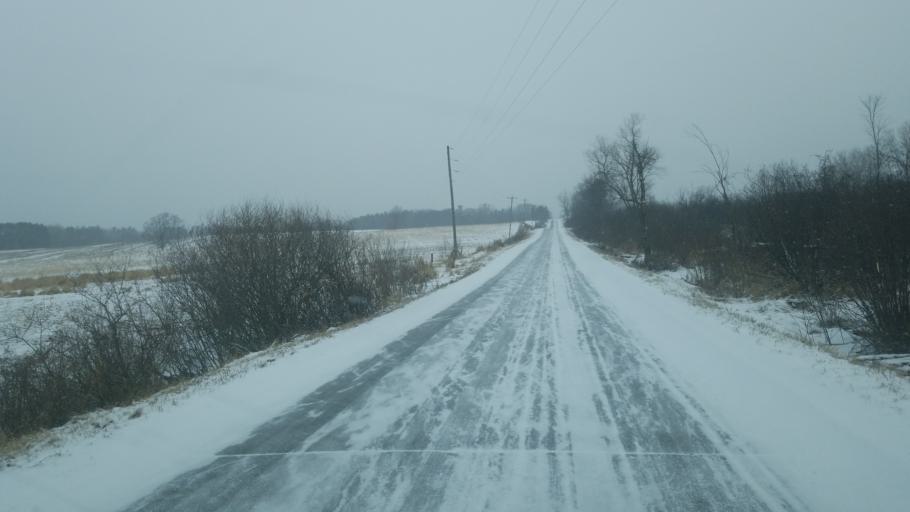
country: US
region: Michigan
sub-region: Mecosta County
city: Big Rapids
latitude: 43.7742
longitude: -85.4028
